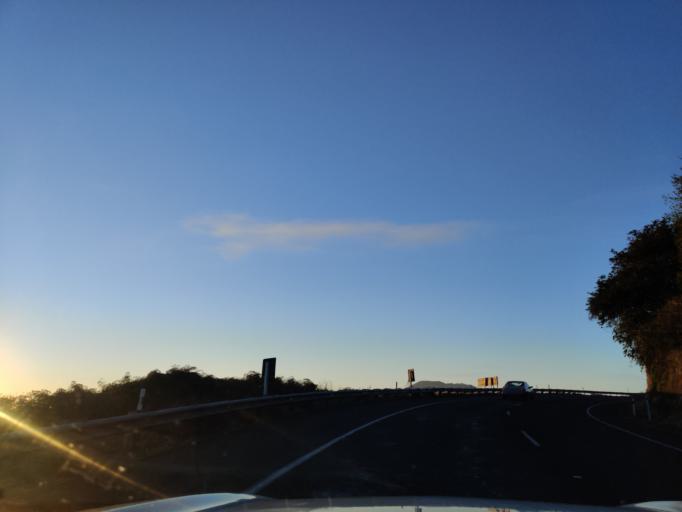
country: NZ
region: Waikato
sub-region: Taupo District
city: Taupo
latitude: -38.6515
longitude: 176.0608
